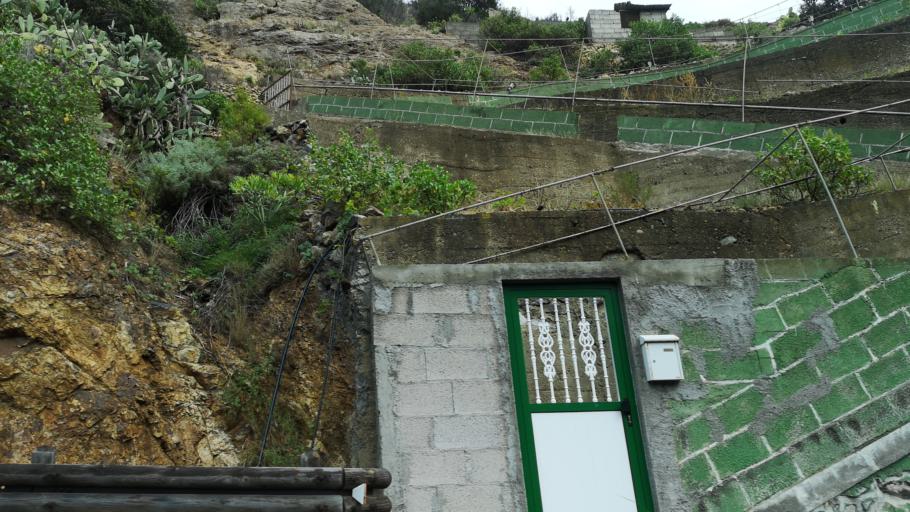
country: ES
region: Canary Islands
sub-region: Provincia de Santa Cruz de Tenerife
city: Vallehermosa
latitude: 28.1720
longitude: -17.2742
